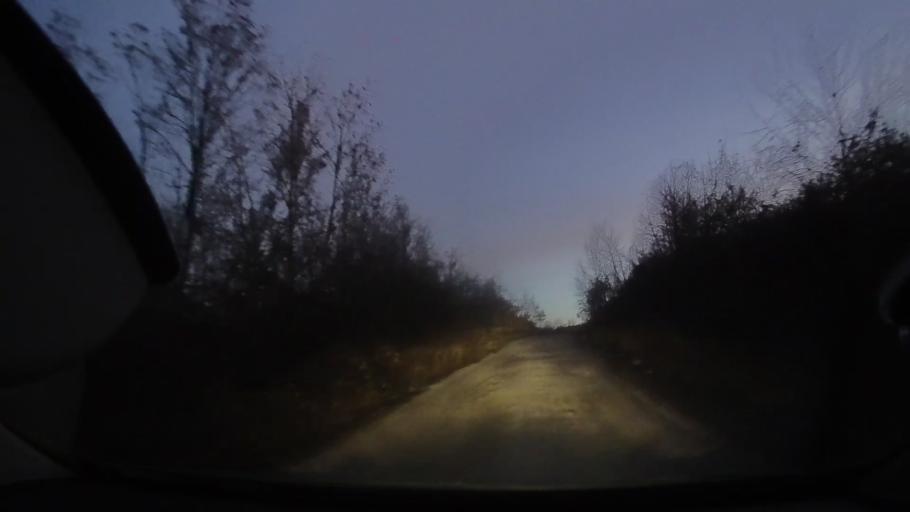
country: RO
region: Bihor
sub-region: Comuna Varciorog
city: Varciorog
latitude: 46.9958
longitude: 22.3077
